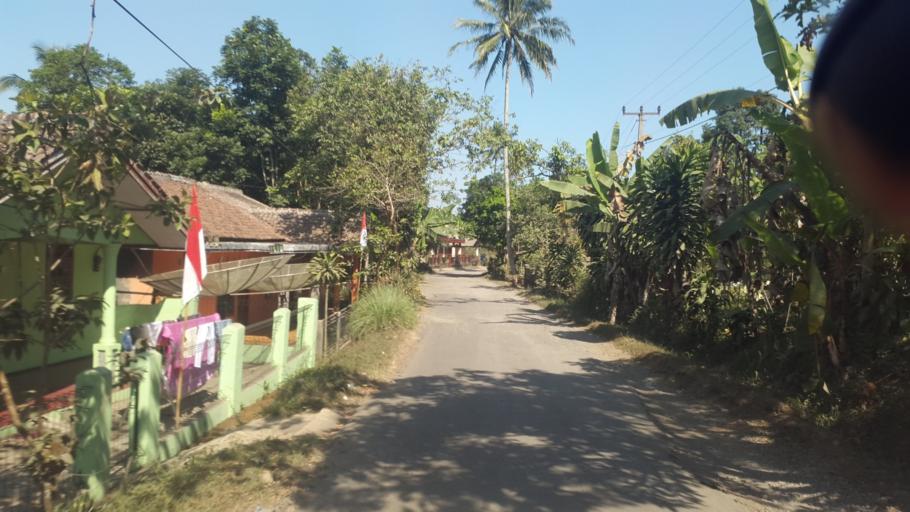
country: ID
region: West Java
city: Cicurug
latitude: -6.8316
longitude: 106.6778
